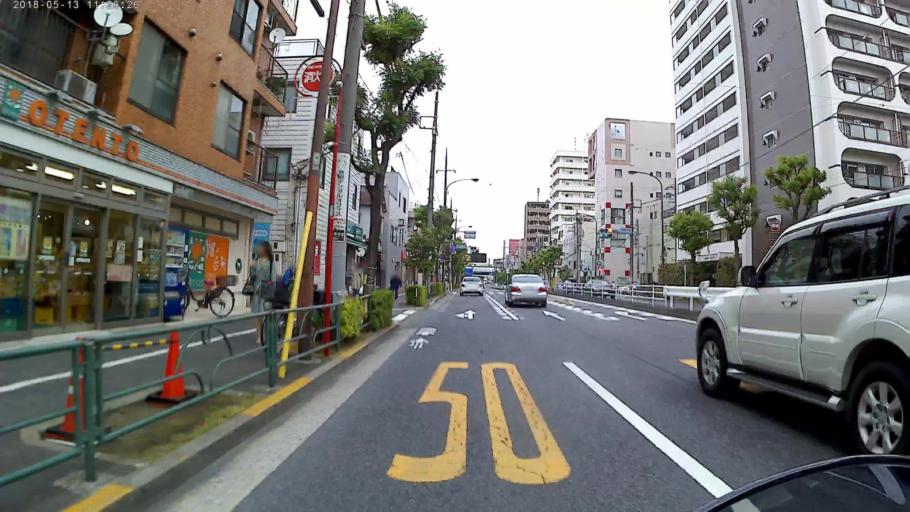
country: JP
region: Kanagawa
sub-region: Kawasaki-shi
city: Kawasaki
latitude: 35.5876
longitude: 139.6747
